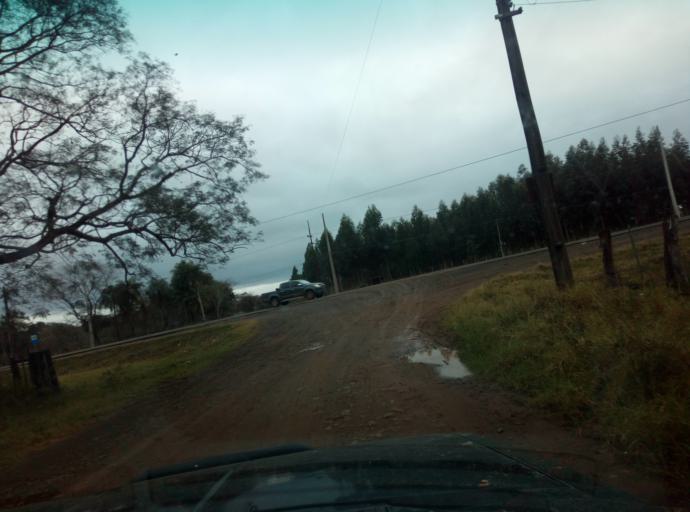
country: PY
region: Caaguazu
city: Carayao
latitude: -25.1901
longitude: -56.3902
